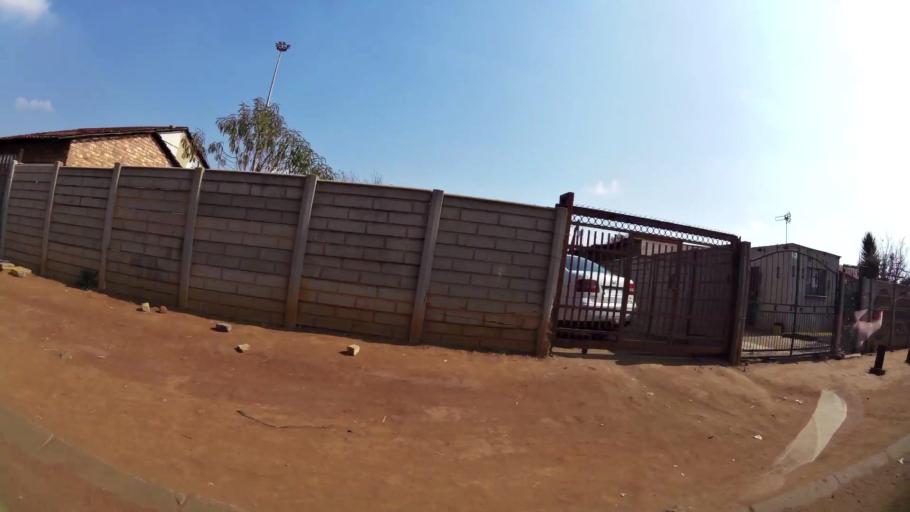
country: ZA
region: Gauteng
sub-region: Ekurhuleni Metropolitan Municipality
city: Springs
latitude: -26.1155
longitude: 28.4836
